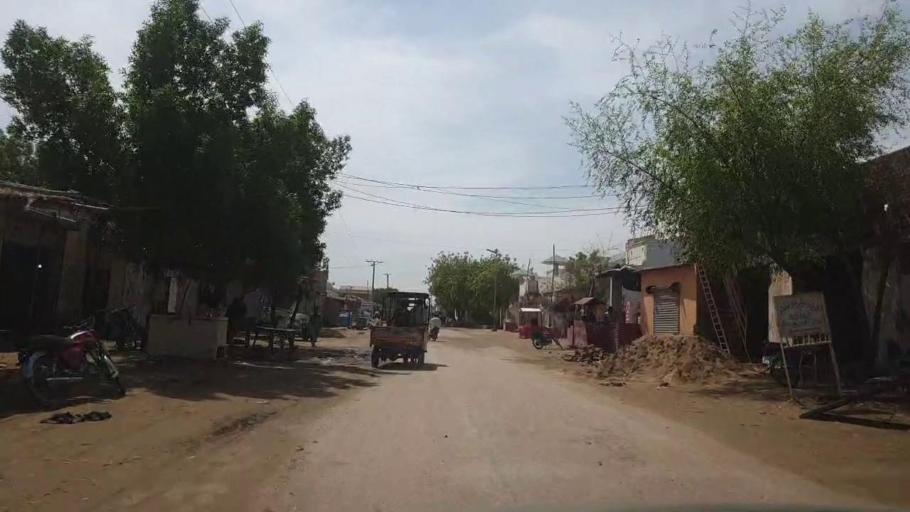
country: PK
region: Sindh
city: Kot Diji
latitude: 27.1572
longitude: 68.9602
